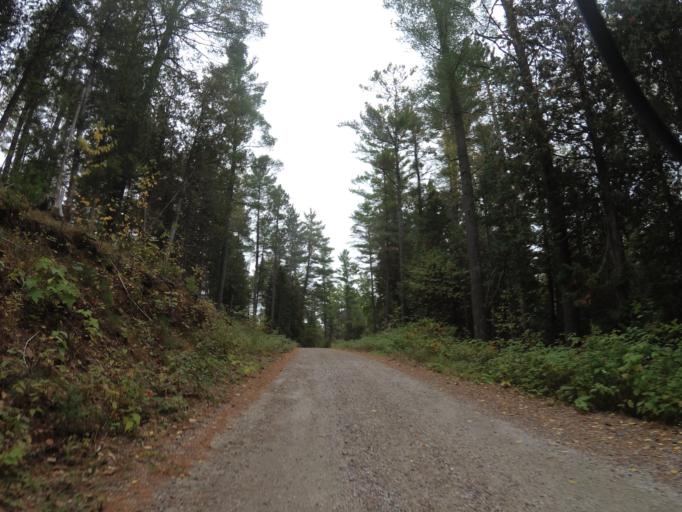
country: CA
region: Ontario
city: Renfrew
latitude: 45.2169
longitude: -77.1205
